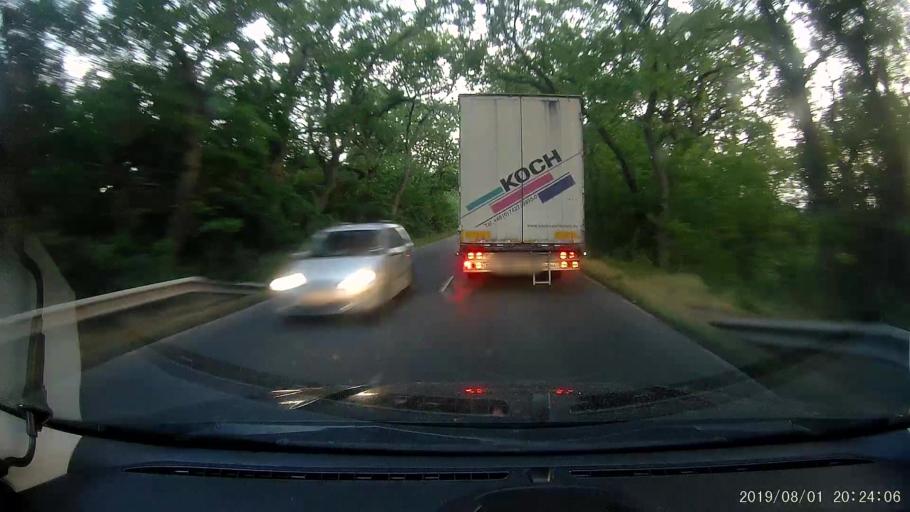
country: BG
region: Yambol
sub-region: Obshtina Elkhovo
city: Elkhovo
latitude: 42.2376
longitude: 26.5958
